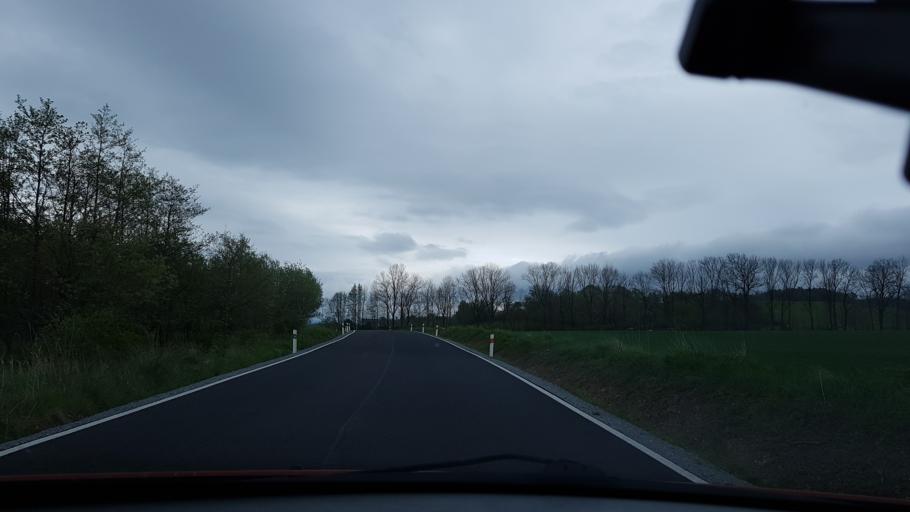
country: PL
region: Opole Voivodeship
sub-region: Powiat nyski
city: Kamienica
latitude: 50.4292
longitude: 16.9552
